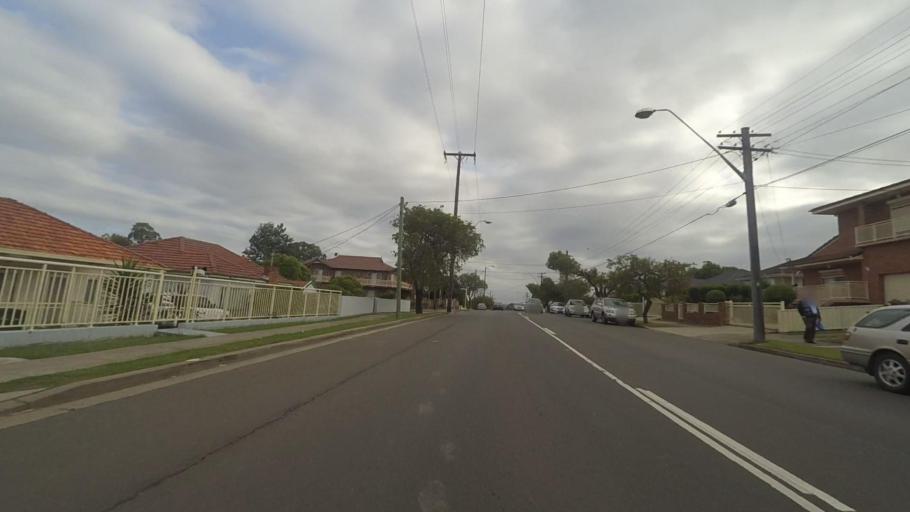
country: AU
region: New South Wales
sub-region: Bankstown
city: Bankstown
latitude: -33.9197
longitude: 151.0135
